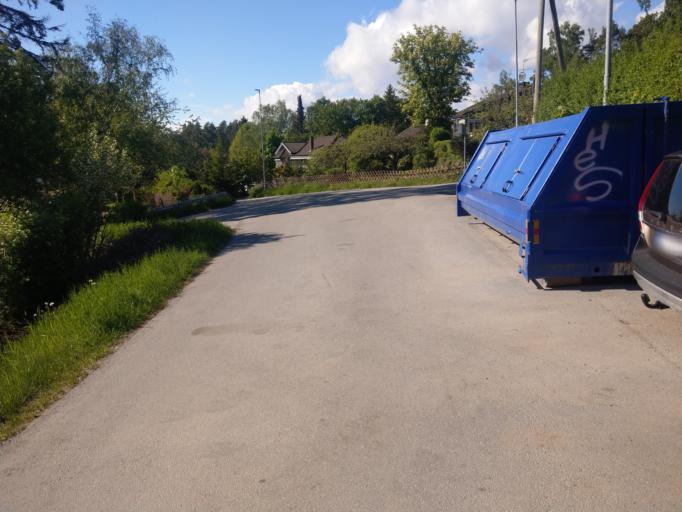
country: SE
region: Stockholm
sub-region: Jarfalla Kommun
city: Jakobsberg
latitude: 59.3926
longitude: 17.8560
